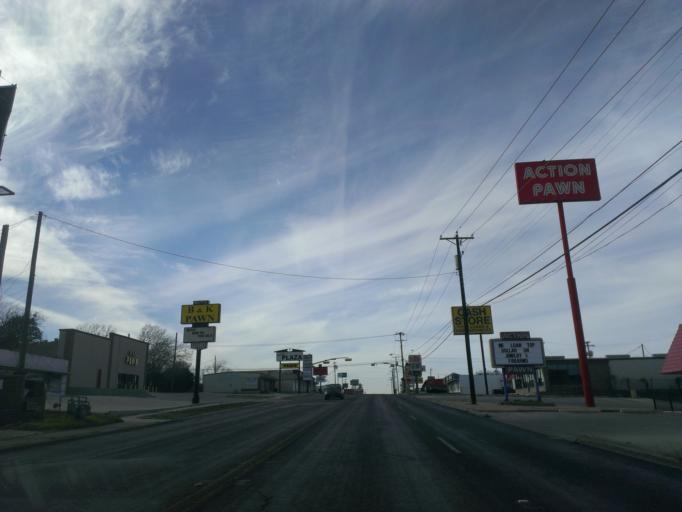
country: US
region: Texas
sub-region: Bell County
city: Killeen
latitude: 31.1282
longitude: -97.7344
